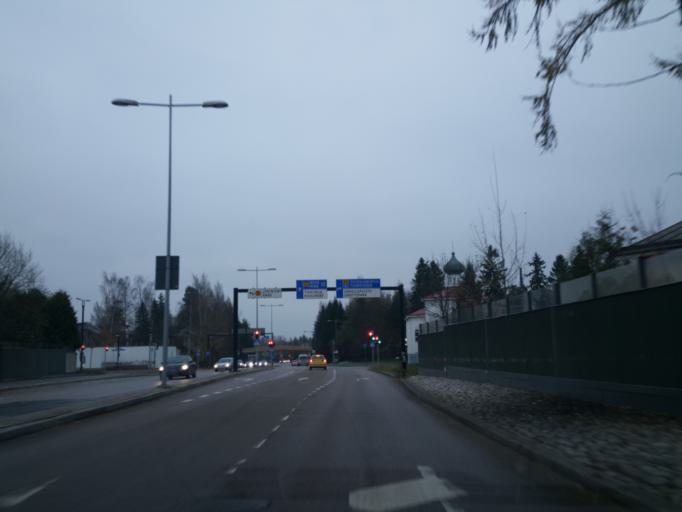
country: FI
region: Uusimaa
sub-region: Helsinki
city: Vantaa
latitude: 60.3004
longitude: 25.0330
